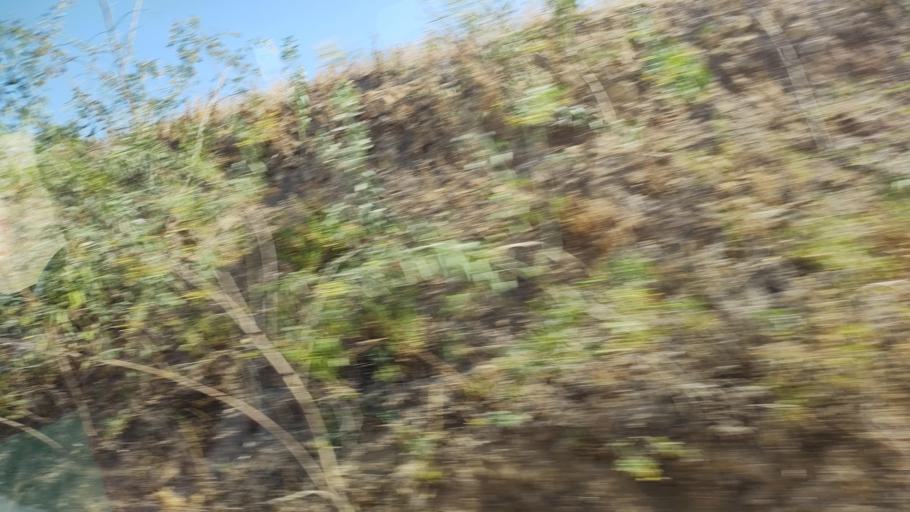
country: ES
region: Andalusia
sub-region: Provincia de Sevilla
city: Aguadulce
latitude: 37.2591
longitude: -4.9830
